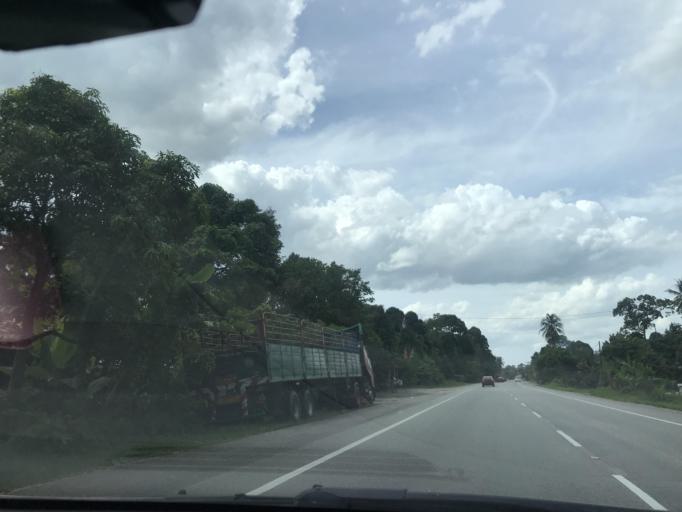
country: MY
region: Kelantan
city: Kampong Pangkal Kalong
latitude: 5.9022
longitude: 102.1861
